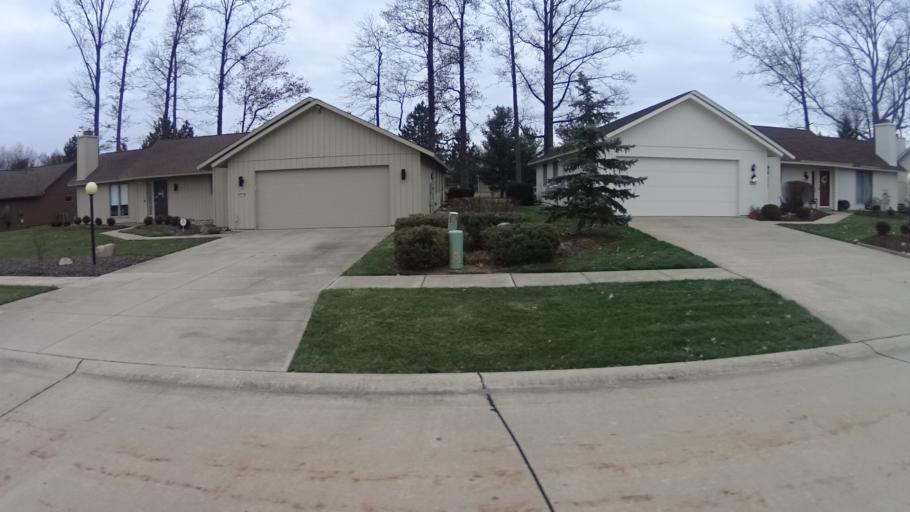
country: US
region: Ohio
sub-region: Lorain County
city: North Ridgeville
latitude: 41.3649
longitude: -81.9797
